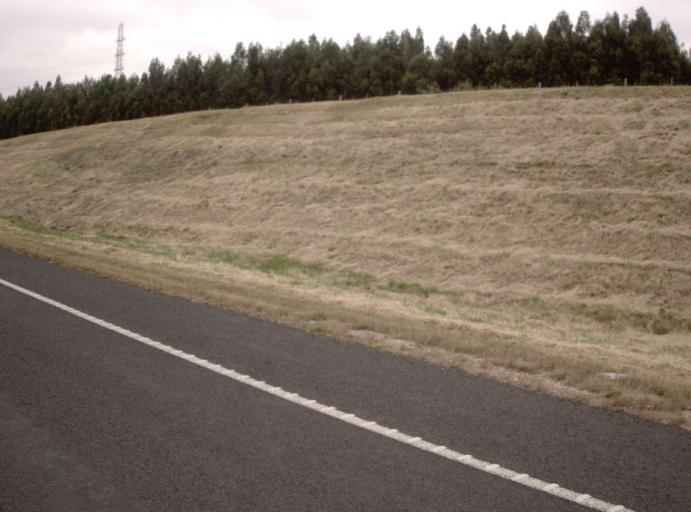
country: AU
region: Victoria
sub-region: Latrobe
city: Morwell
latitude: -38.2460
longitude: 146.3347
